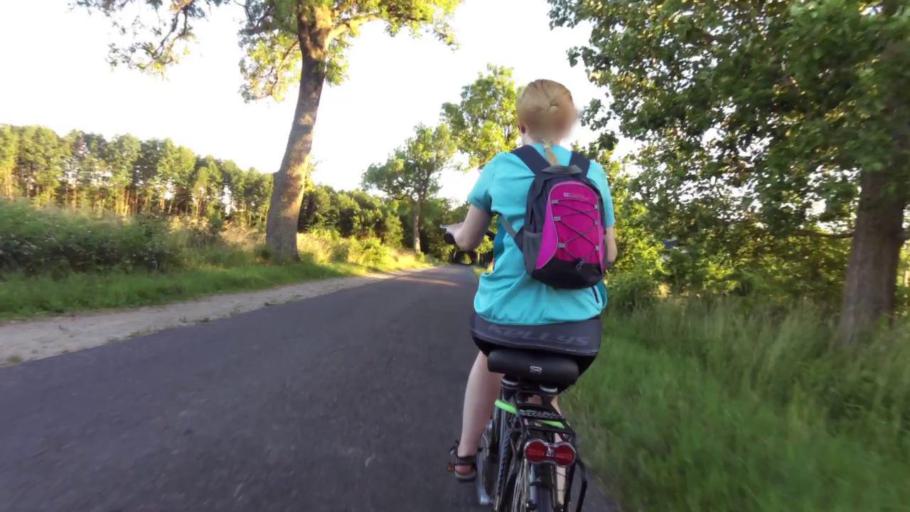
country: PL
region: West Pomeranian Voivodeship
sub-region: Powiat bialogardzki
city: Bialogard
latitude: 54.0459
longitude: 16.0543
